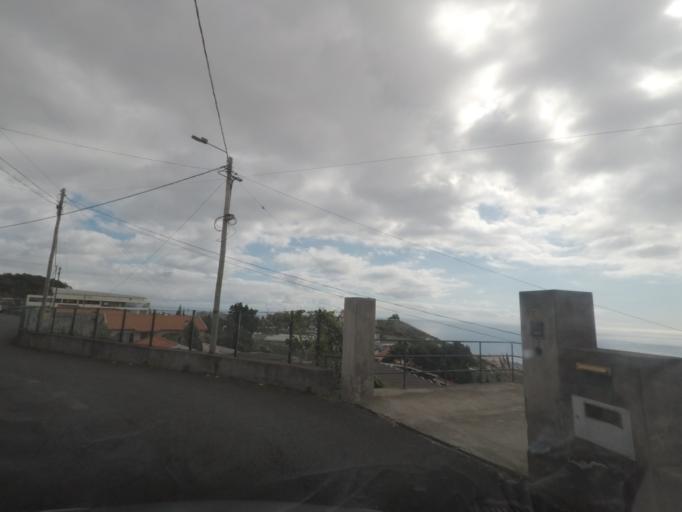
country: PT
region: Madeira
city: Camara de Lobos
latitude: 32.6544
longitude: -16.9466
